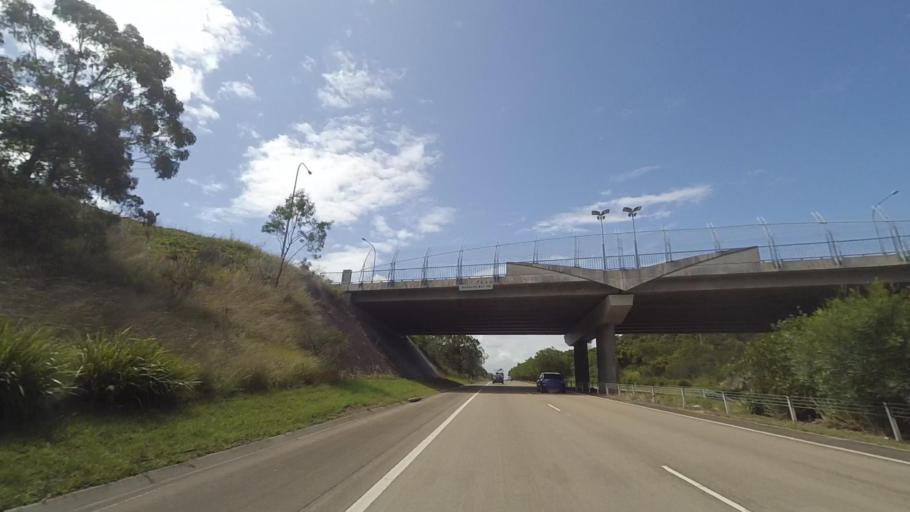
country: AU
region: New South Wales
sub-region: Lake Macquarie Shire
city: Gateshead
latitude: -32.9752
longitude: 151.6780
